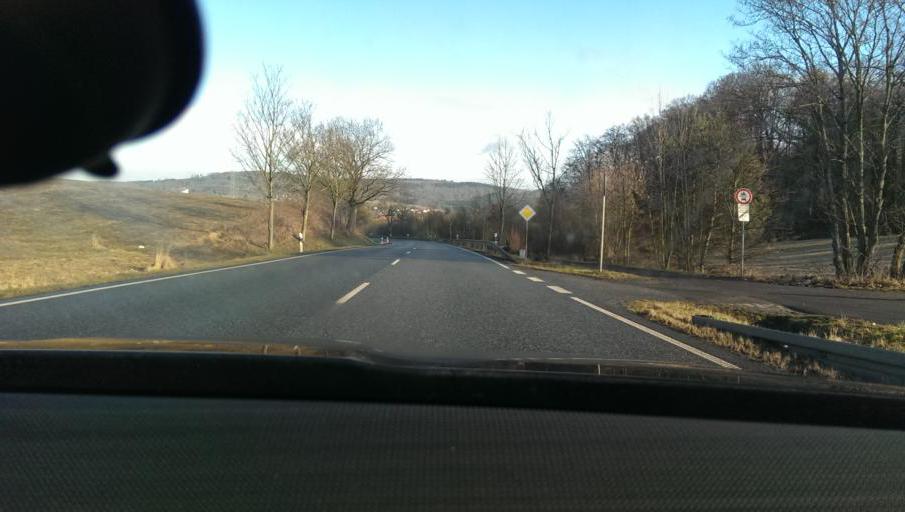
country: DE
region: Hesse
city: Hain-Grundau
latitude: 50.2272
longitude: 9.1408
